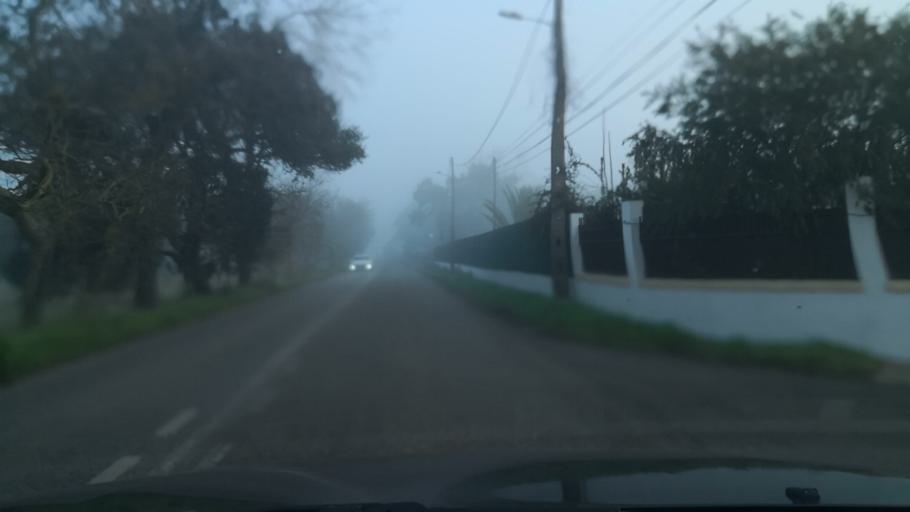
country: PT
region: Setubal
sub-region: Setubal
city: Setubal
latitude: 38.5580
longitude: -8.8386
